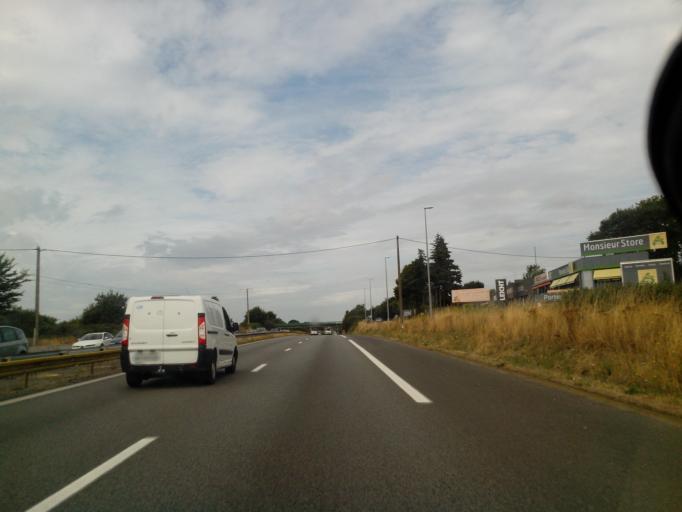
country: FR
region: Brittany
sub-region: Departement du Morbihan
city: Plescop
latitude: 47.6607
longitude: -2.8067
